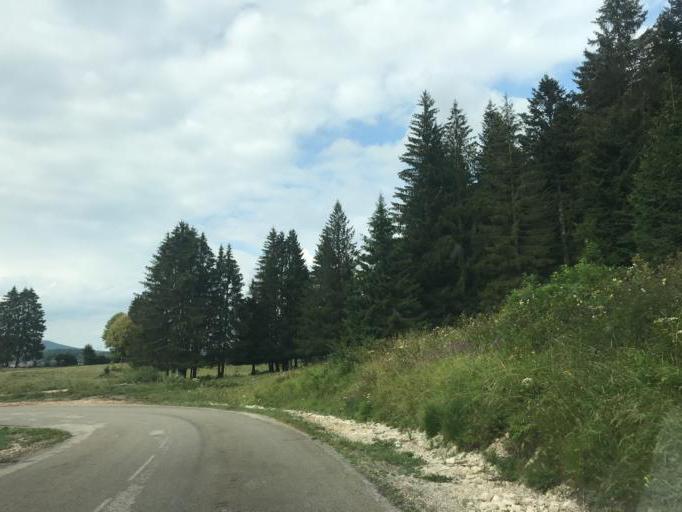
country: FR
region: Franche-Comte
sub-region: Departement du Jura
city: Longchaumois
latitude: 46.5090
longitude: 5.8865
